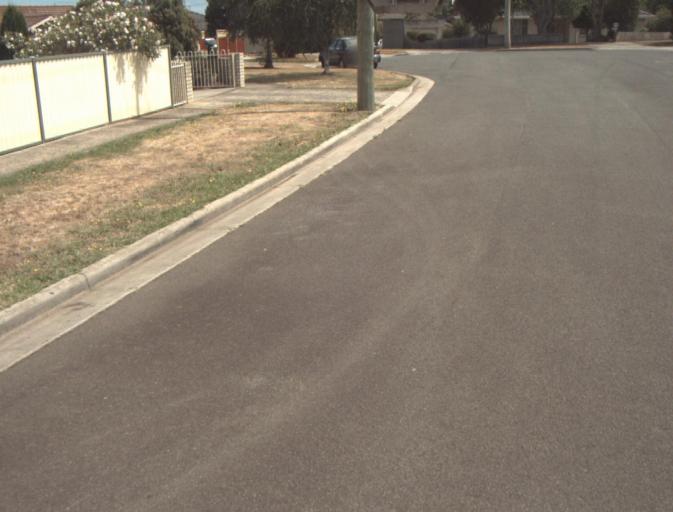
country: AU
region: Tasmania
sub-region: Launceston
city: Mayfield
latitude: -41.3840
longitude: 147.1213
